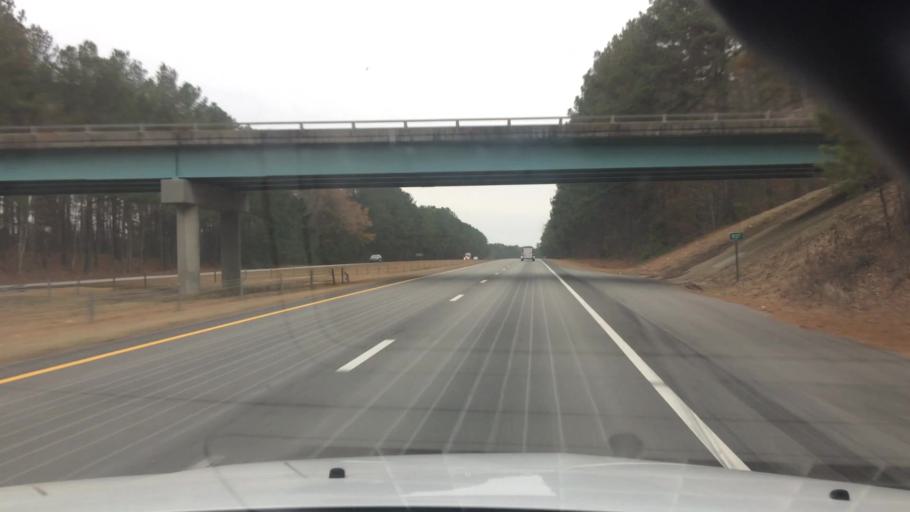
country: US
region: North Carolina
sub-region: Nash County
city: Spring Hope
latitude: 35.9011
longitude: -78.1843
